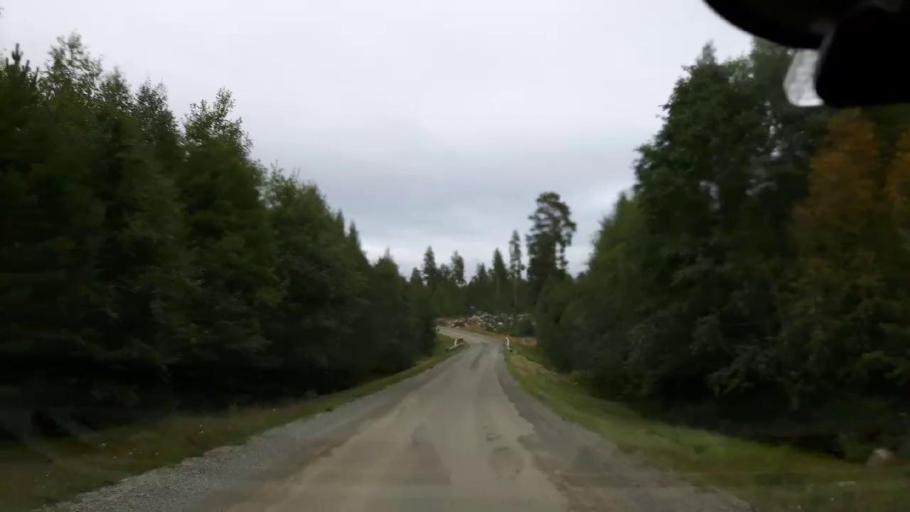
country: SE
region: Vaesternorrland
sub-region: Ange Kommun
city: Fransta
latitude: 62.8542
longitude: 16.0202
